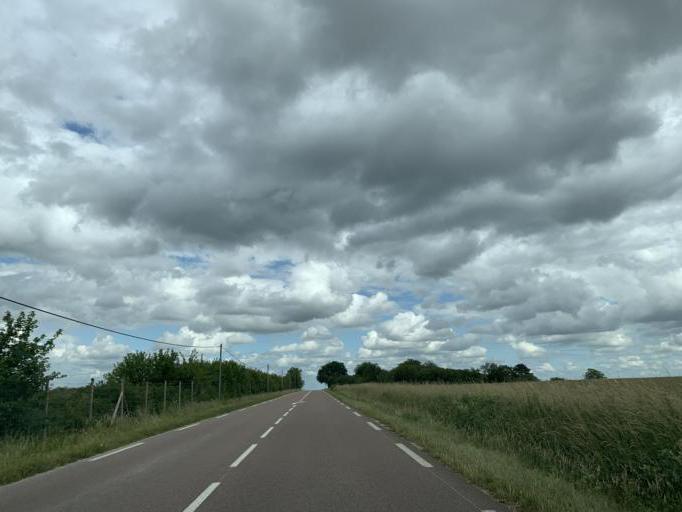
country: FR
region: Bourgogne
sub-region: Departement de l'Yonne
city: Vermenton
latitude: 47.7389
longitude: 3.7540
